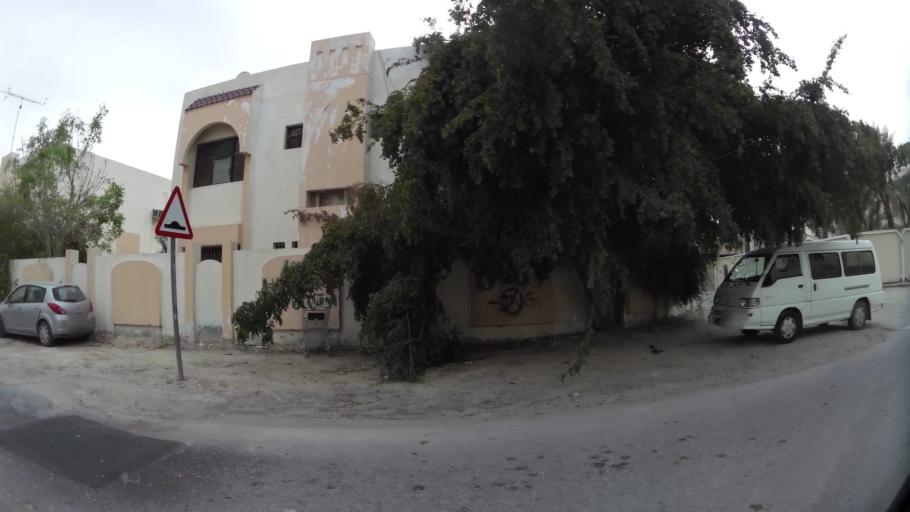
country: QA
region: Baladiyat ad Dawhah
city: Doha
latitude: 25.3068
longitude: 51.4923
